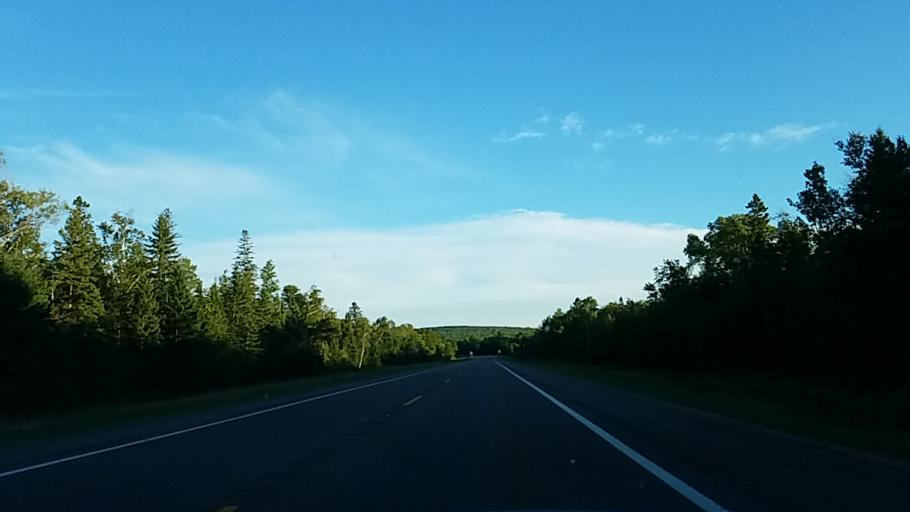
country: US
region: Michigan
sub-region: Alger County
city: Munising
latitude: 46.4487
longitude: -86.8881
